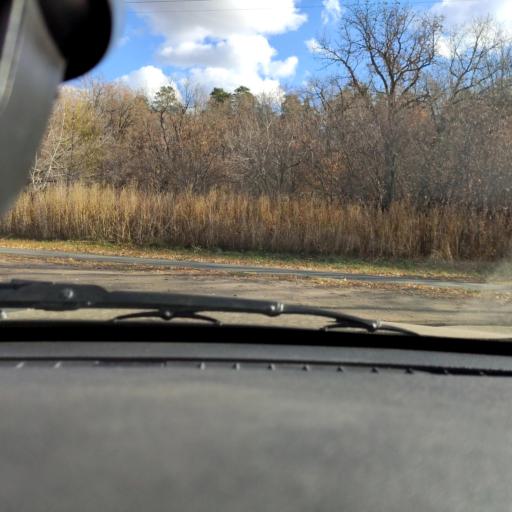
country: RU
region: Samara
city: Tol'yatti
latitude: 53.5078
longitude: 49.3069
